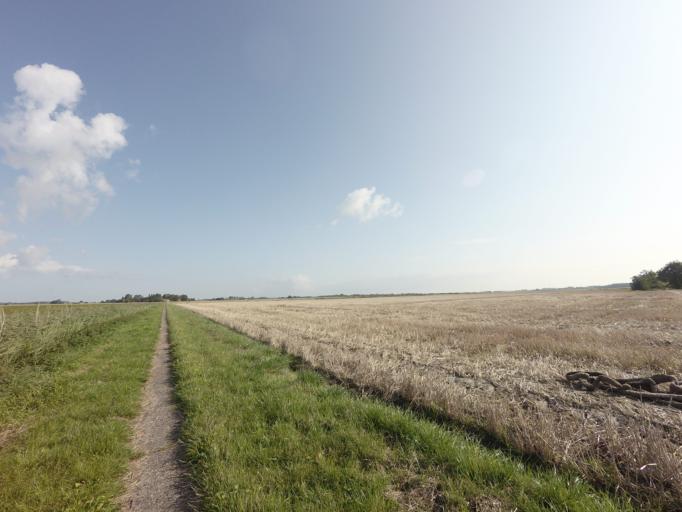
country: NL
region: Friesland
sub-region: Gemeente Franekeradeel
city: Franeker
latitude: 53.2037
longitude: 5.5644
